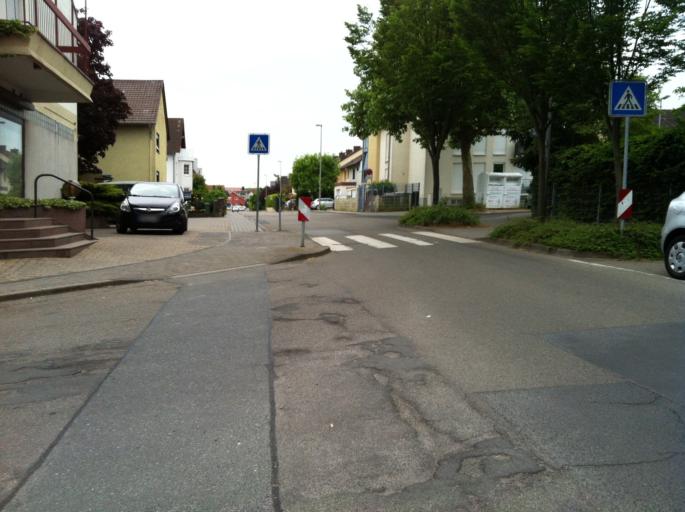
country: DE
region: Rheinland-Pfalz
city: Budenheim
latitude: 49.9851
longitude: 8.1688
